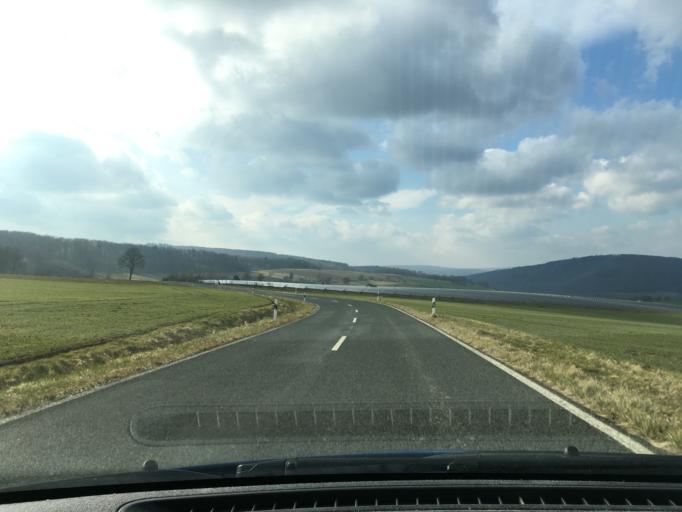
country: DE
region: Lower Saxony
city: Uslar
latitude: 51.6076
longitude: 9.6376
